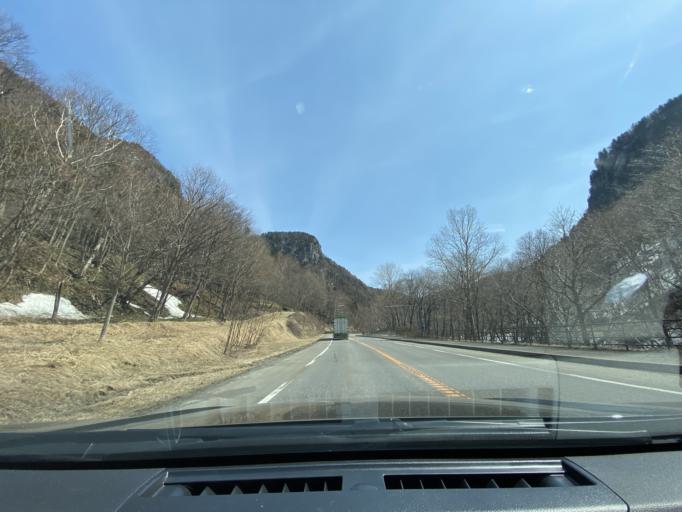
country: JP
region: Hokkaido
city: Kamikawa
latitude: 43.7253
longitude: 142.9685
